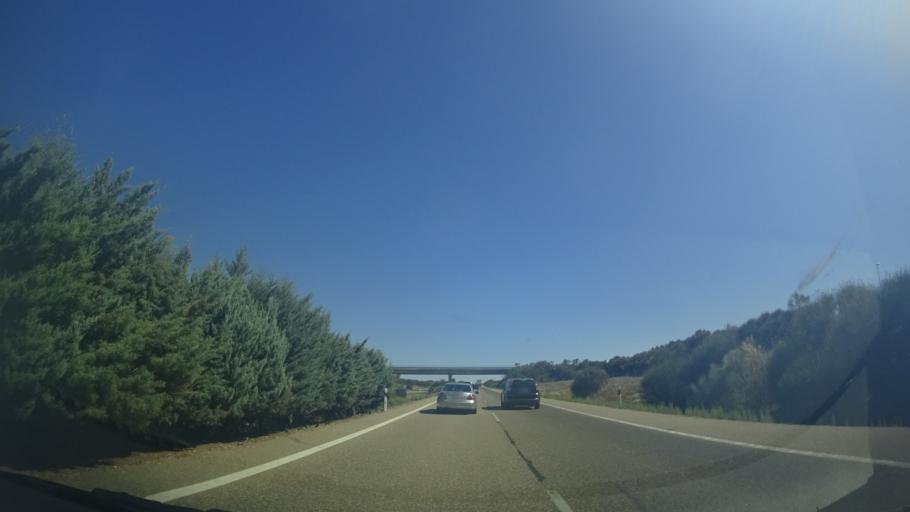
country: ES
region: Castille and Leon
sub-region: Provincia de Zamora
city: Villalpando
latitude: 41.8288
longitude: -5.3795
